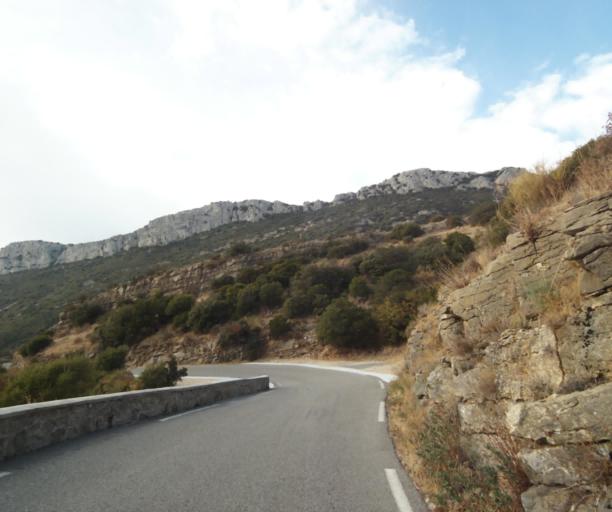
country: FR
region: Provence-Alpes-Cote d'Azur
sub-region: Departement des Bouches-du-Rhone
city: Gemenos
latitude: 43.3124
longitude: 5.6670
